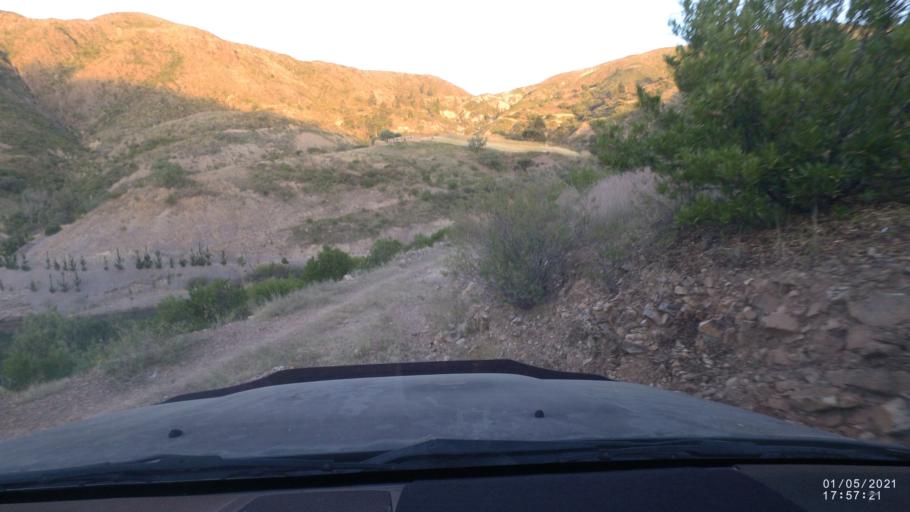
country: BO
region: Cochabamba
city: Capinota
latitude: -17.6860
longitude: -66.1691
